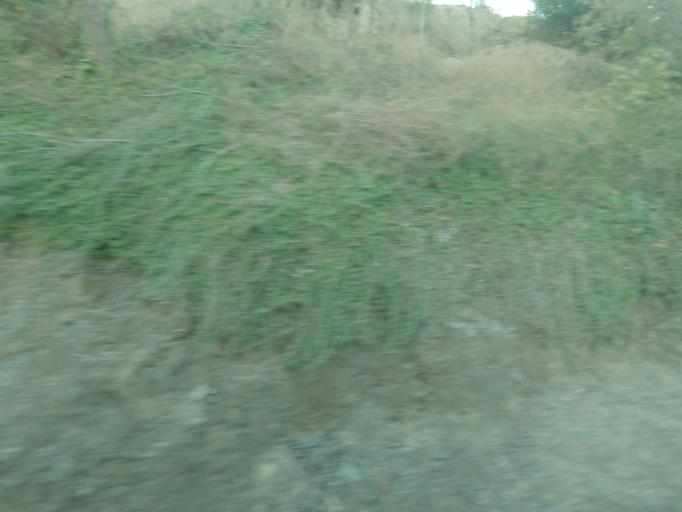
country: PT
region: Vila Real
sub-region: Santa Marta de Penaguiao
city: Santa Marta de Penaguiao
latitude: 41.1977
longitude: -7.7650
